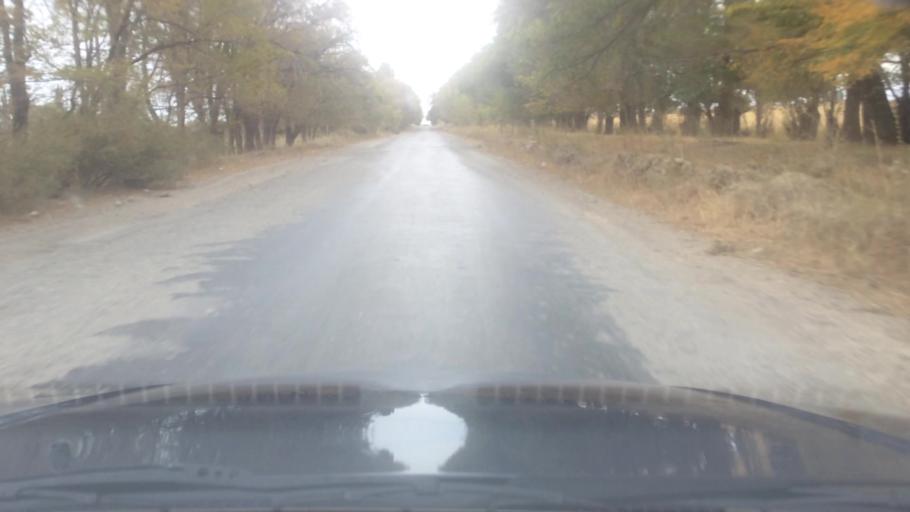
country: KG
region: Ysyk-Koel
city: Balykchy
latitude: 42.3041
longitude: 76.4763
